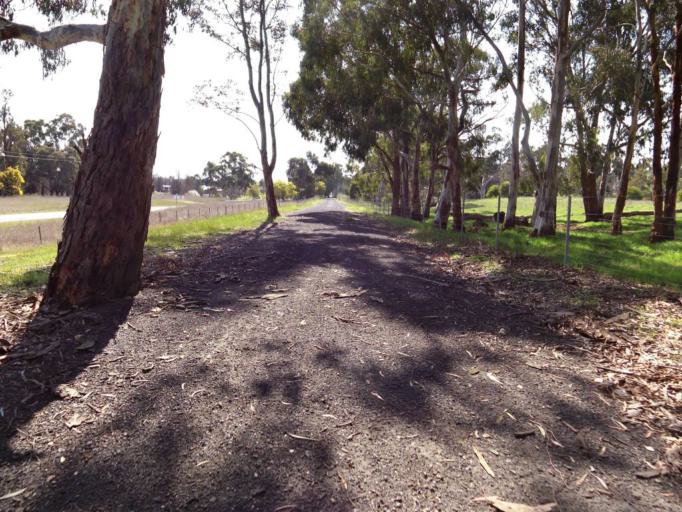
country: AU
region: Victoria
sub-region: Murrindindi
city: Alexandra
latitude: -37.1306
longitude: 145.5945
